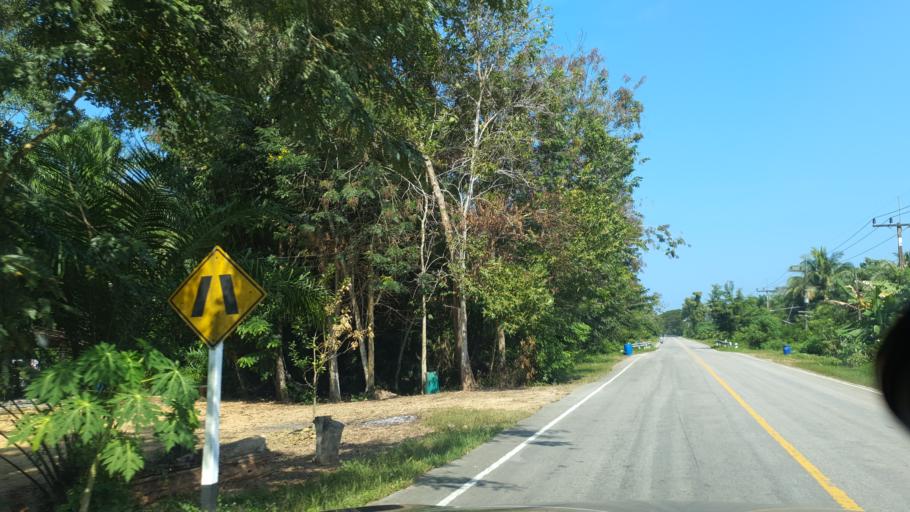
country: TH
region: Surat Thani
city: Tha Chana
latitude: 9.5797
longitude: 99.1905
